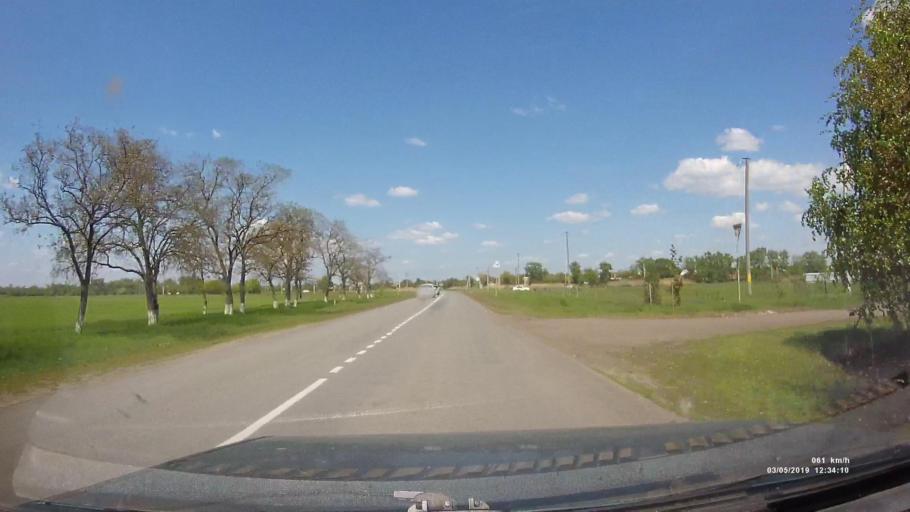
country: RU
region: Rostov
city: Semikarakorsk
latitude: 47.5198
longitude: 40.7694
